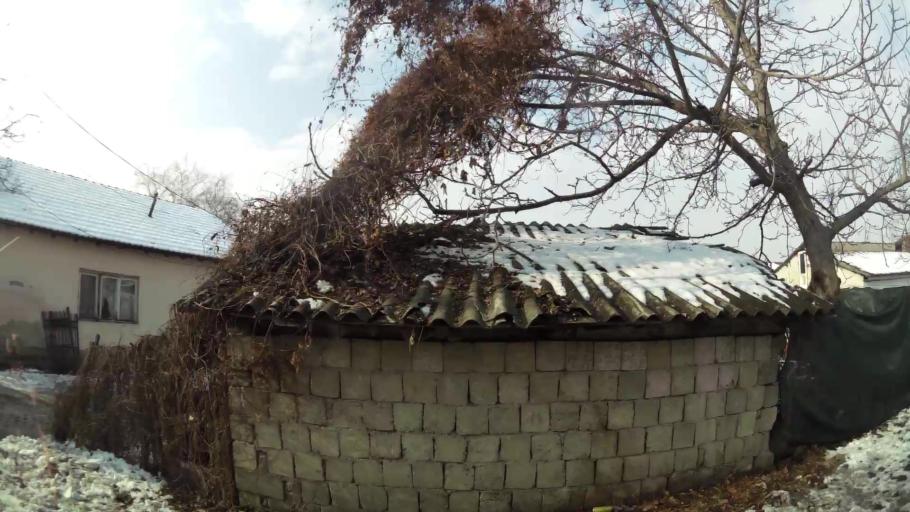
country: MK
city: Krushopek
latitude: 42.0165
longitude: 21.3830
